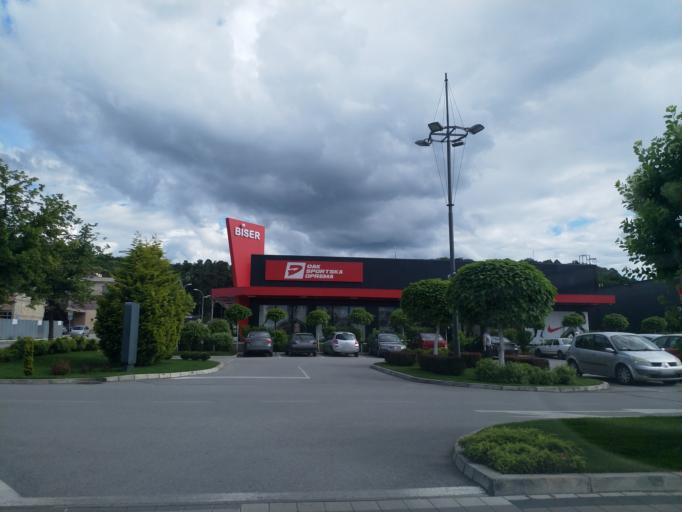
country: RS
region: Central Serbia
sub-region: Pomoravski Okrug
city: Jagodina
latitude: 43.9669
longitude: 21.2653
